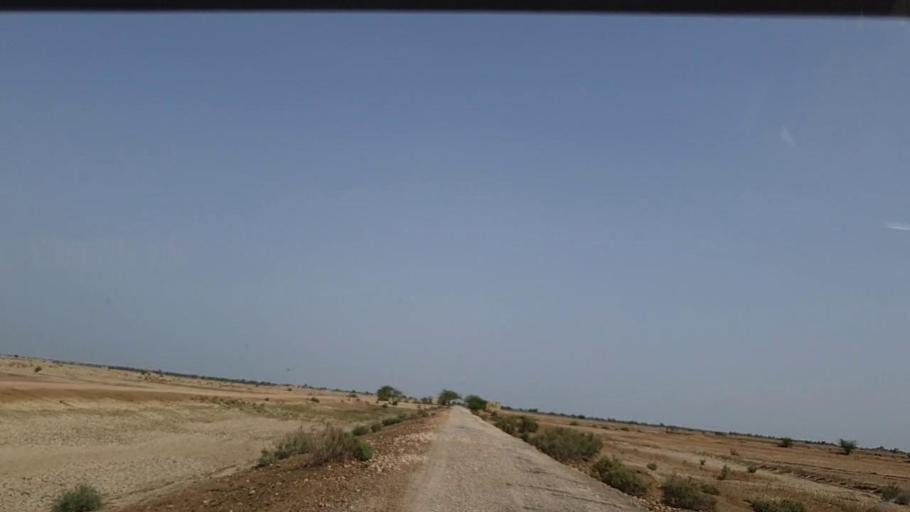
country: PK
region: Sindh
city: Johi
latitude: 26.7672
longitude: 67.6593
